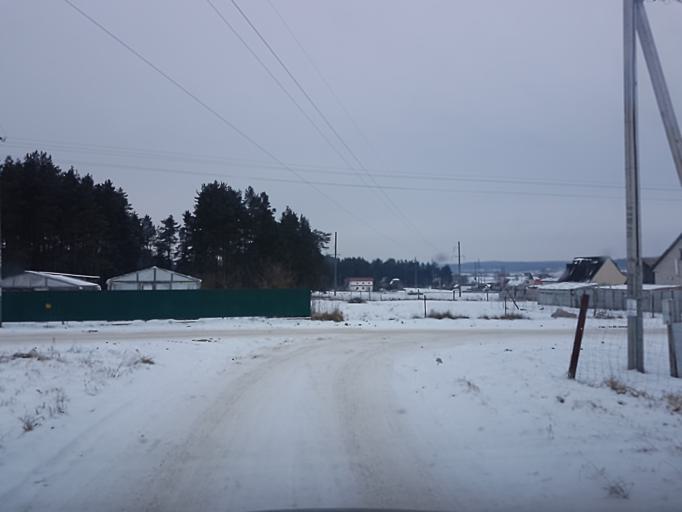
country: BY
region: Minsk
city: Rakaw
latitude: 53.9645
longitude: 27.0380
